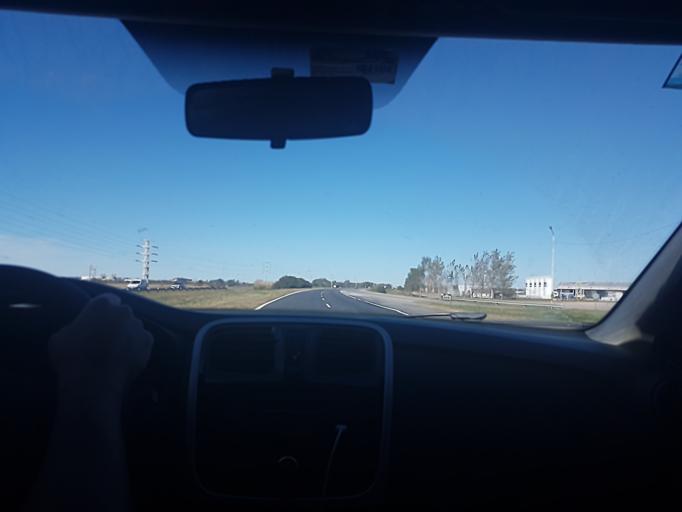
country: AR
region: Cordoba
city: Pilar
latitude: -31.6515
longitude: -63.8564
